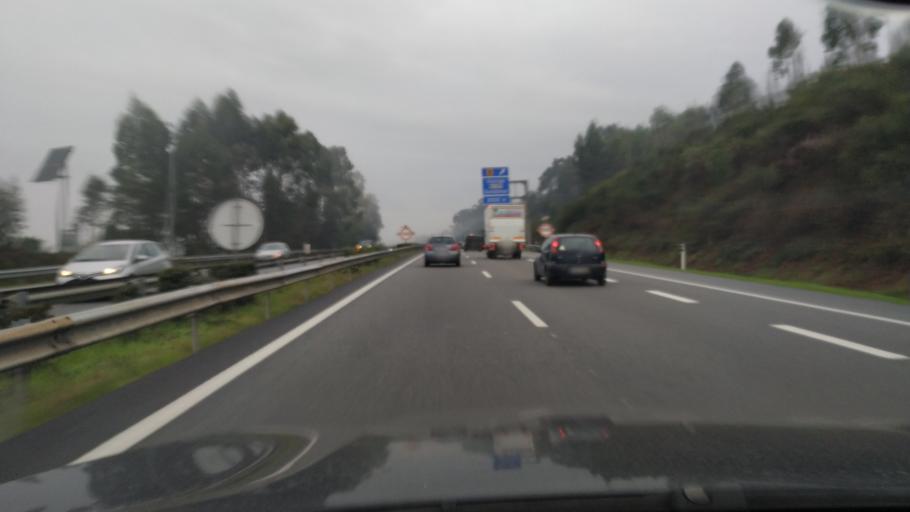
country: PT
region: Porto
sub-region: Valongo
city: Campo
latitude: 41.1921
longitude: -8.4822
